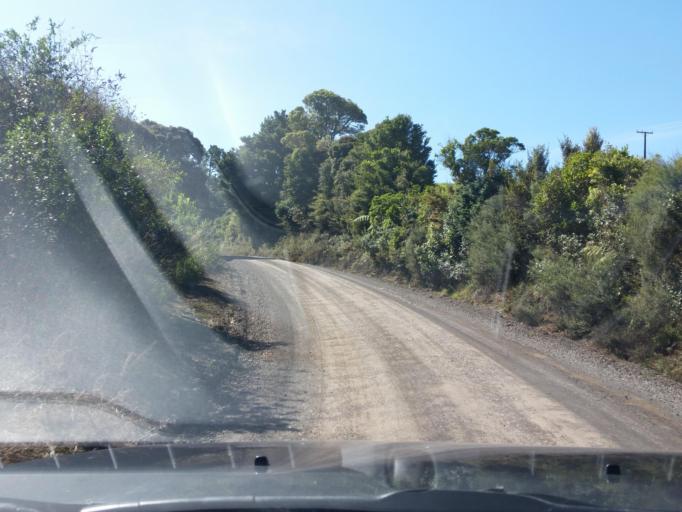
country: NZ
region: Northland
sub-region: Kaipara District
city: Dargaville
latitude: -35.7133
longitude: 173.6321
